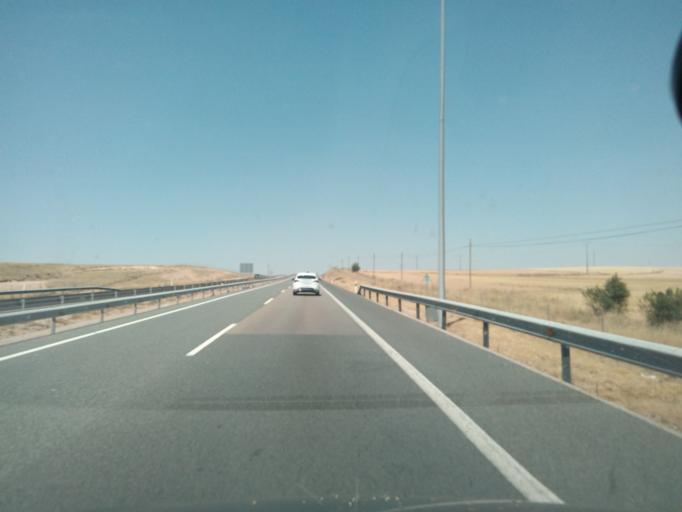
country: ES
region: Castille-La Mancha
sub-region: Province of Toledo
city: Tembleque
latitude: 39.7080
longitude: -3.4967
